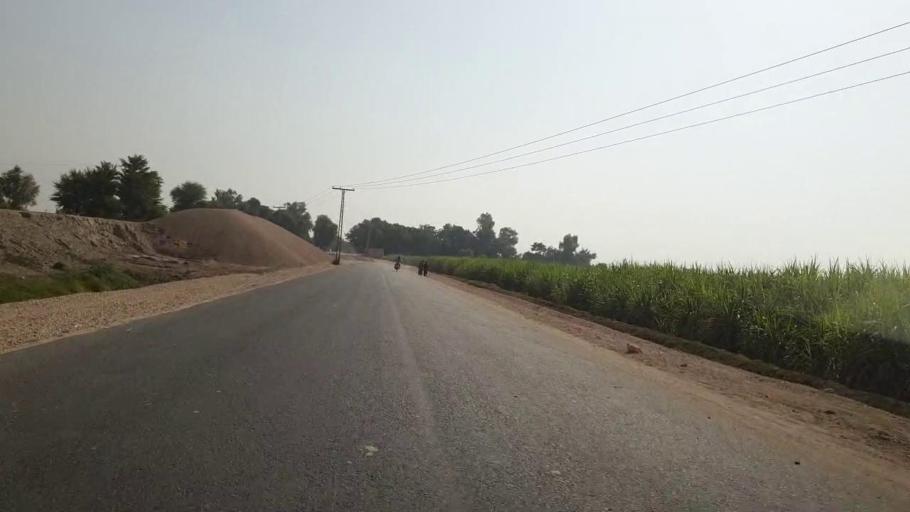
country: PK
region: Sindh
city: Bhan
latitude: 26.6017
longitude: 67.7792
